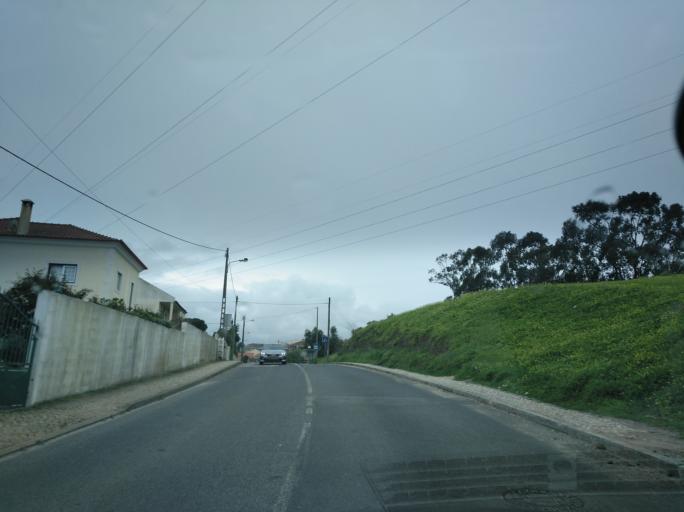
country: PT
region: Lisbon
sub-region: Odivelas
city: Ramada
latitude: 38.7906
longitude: -9.1966
